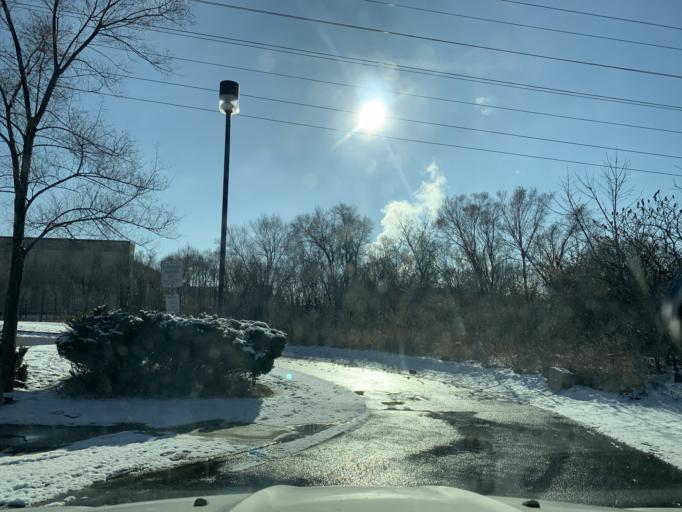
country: CA
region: Ontario
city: Toronto
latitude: 43.6762
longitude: -79.4732
